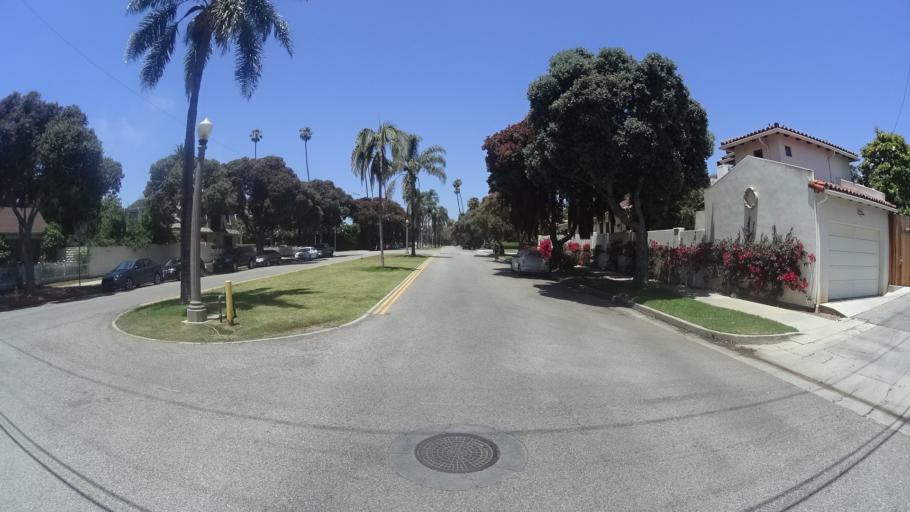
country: US
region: California
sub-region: Los Angeles County
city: Santa Monica
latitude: 34.0249
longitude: -118.5051
